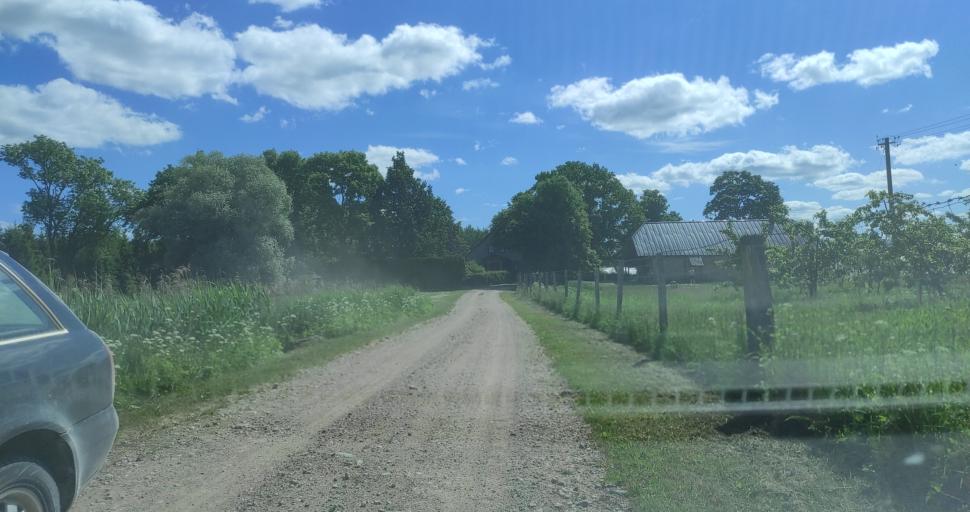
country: LV
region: Aizpute
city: Aizpute
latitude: 56.8700
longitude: 21.7180
